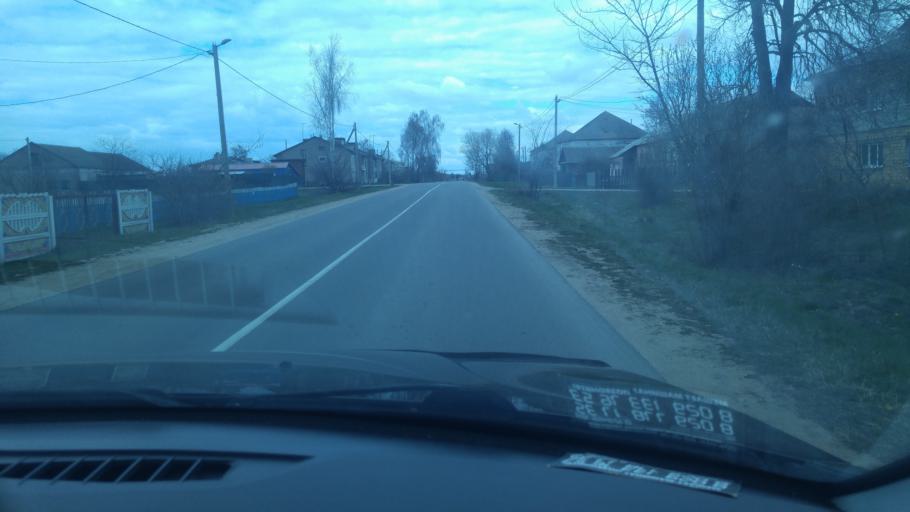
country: BY
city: Michanovichi
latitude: 53.6686
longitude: 27.7486
